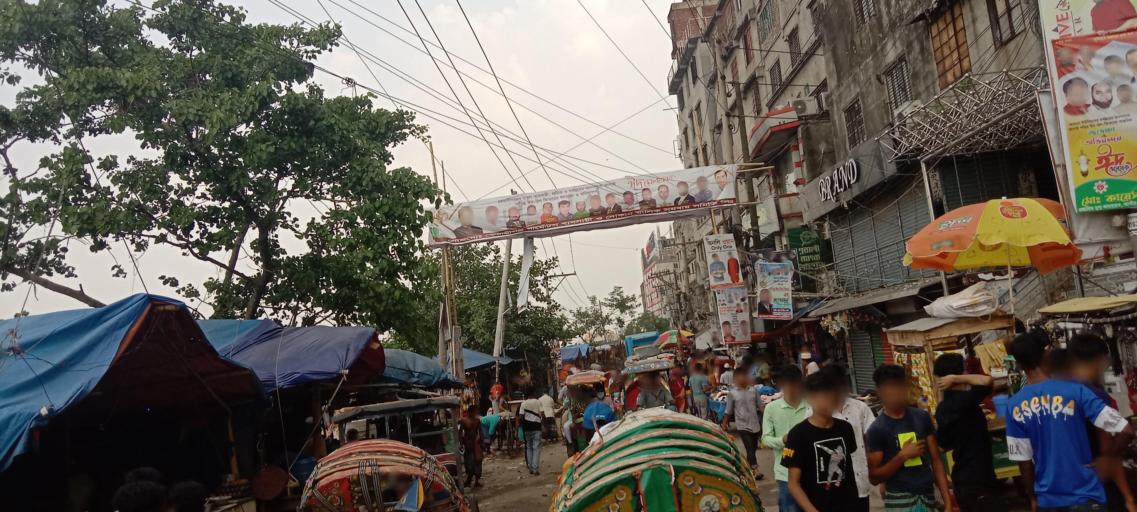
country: BD
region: Dhaka
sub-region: Dhaka
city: Dhaka
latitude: 23.7035
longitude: 90.4076
